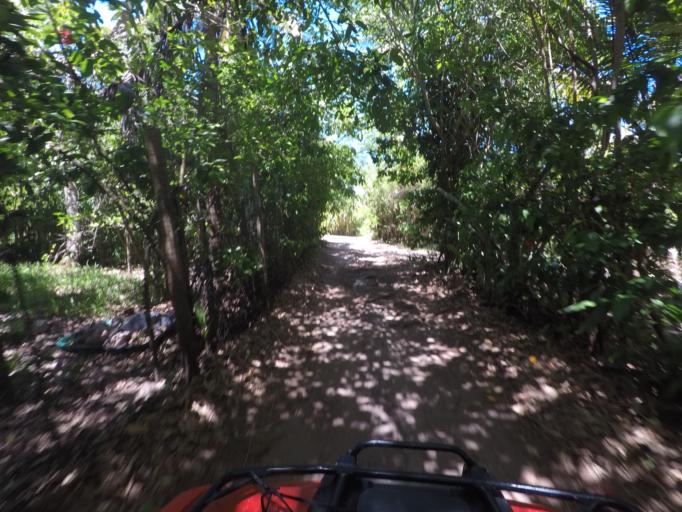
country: BR
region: Bahia
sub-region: Marau
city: Marau
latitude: -13.9966
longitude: -38.9443
